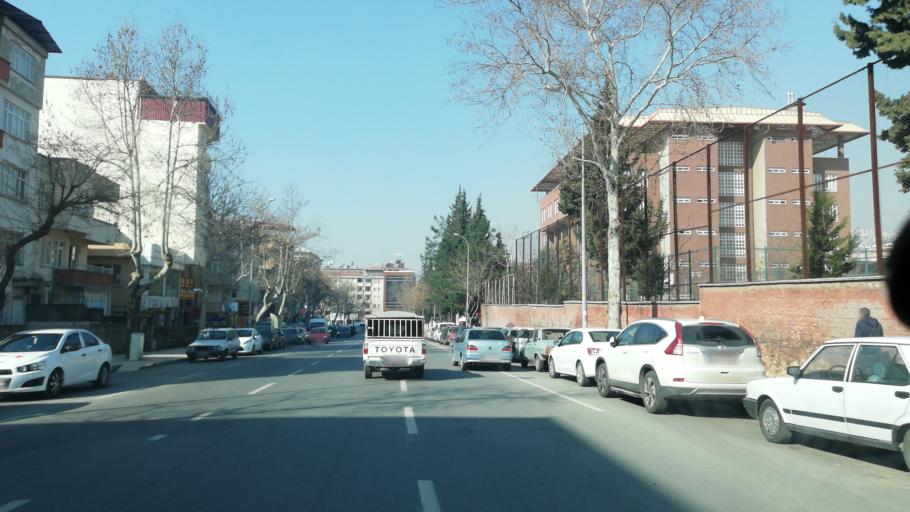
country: TR
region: Kahramanmaras
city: Kahramanmaras
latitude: 37.5723
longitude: 36.9281
